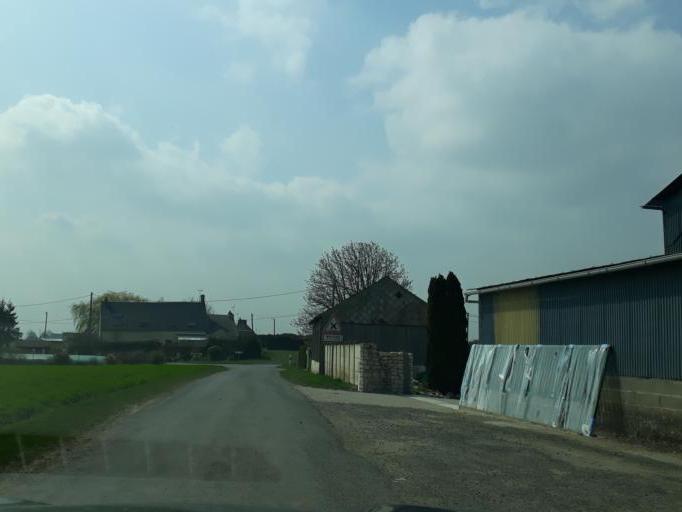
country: FR
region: Centre
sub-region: Departement d'Eure-et-Loir
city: Baigneaux
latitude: 48.0867
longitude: 1.8122
